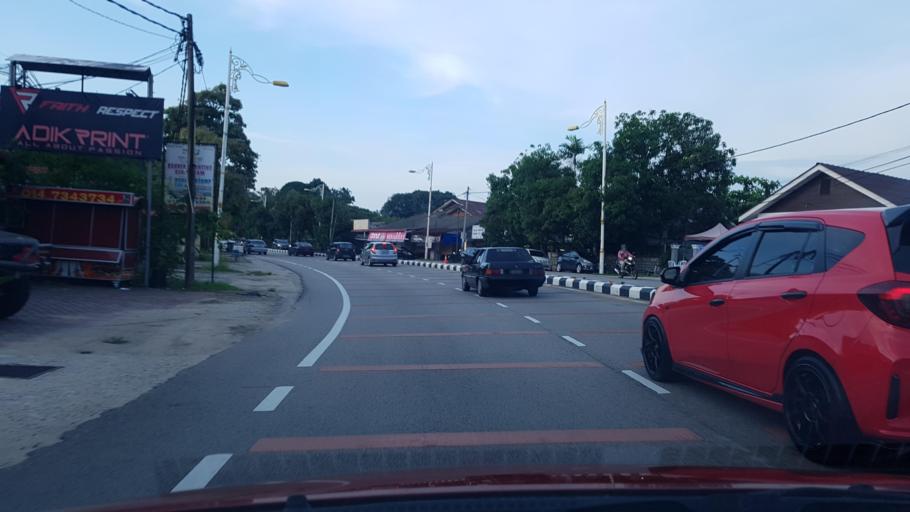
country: MY
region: Terengganu
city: Kuala Terengganu
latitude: 5.3170
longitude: 103.1517
